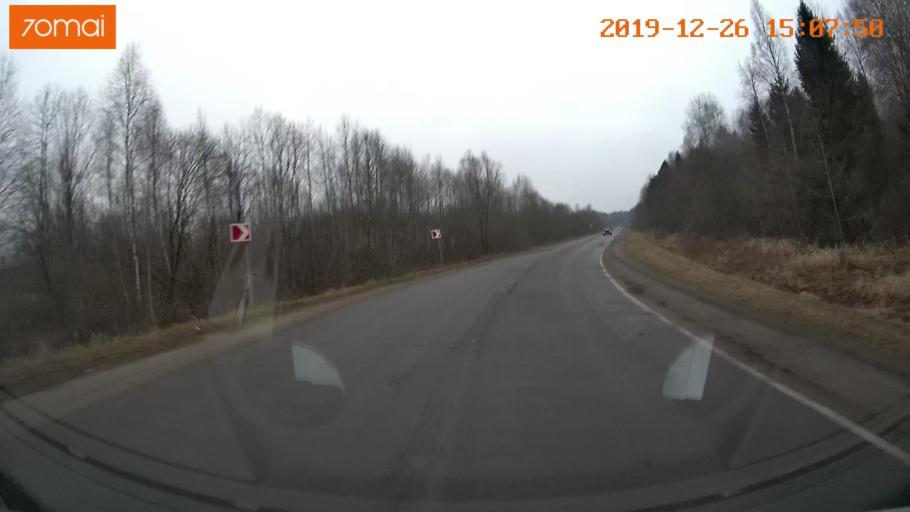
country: RU
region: Jaroslavl
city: Rybinsk
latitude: 58.1659
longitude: 38.8423
